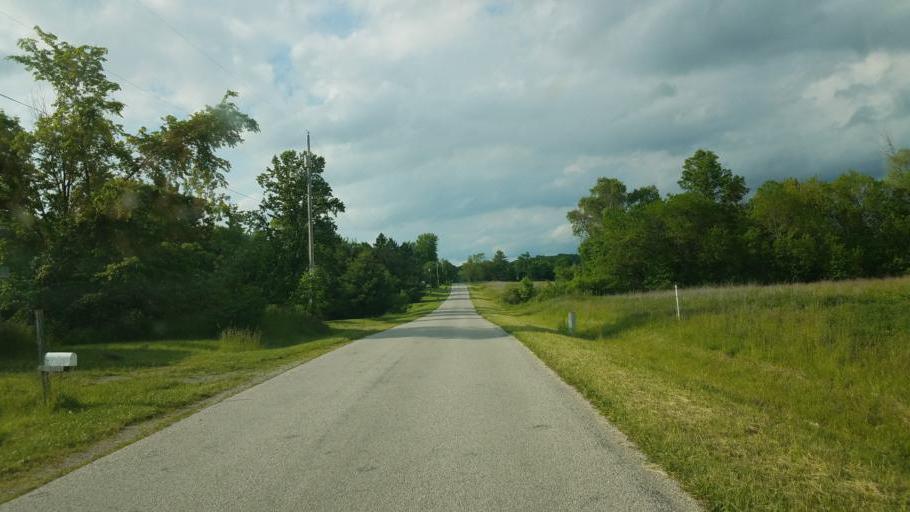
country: US
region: Ohio
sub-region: Knox County
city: Centerburg
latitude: 40.3879
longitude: -82.7609
